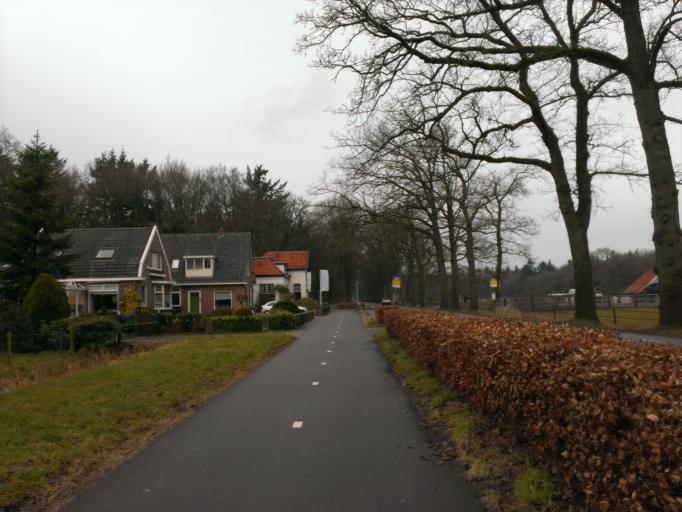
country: NL
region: Drenthe
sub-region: Gemeente Hoogeveen
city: Hoogeveen
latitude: 52.7477
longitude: 6.4682
